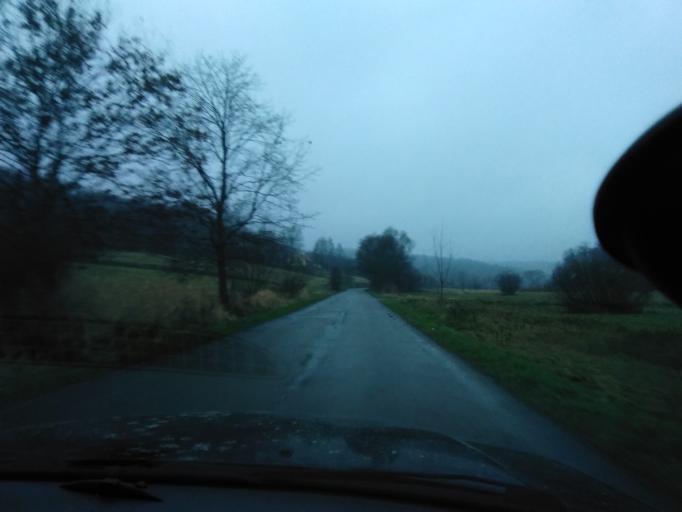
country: PL
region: Subcarpathian Voivodeship
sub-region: Powiat brzozowski
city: Jablonka
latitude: 49.7405
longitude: 22.1489
